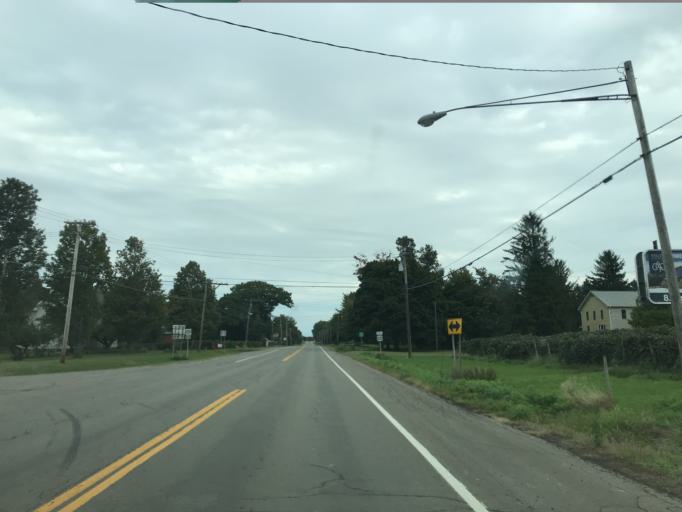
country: US
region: Pennsylvania
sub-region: Erie County
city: North East
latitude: 42.2547
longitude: -79.7392
